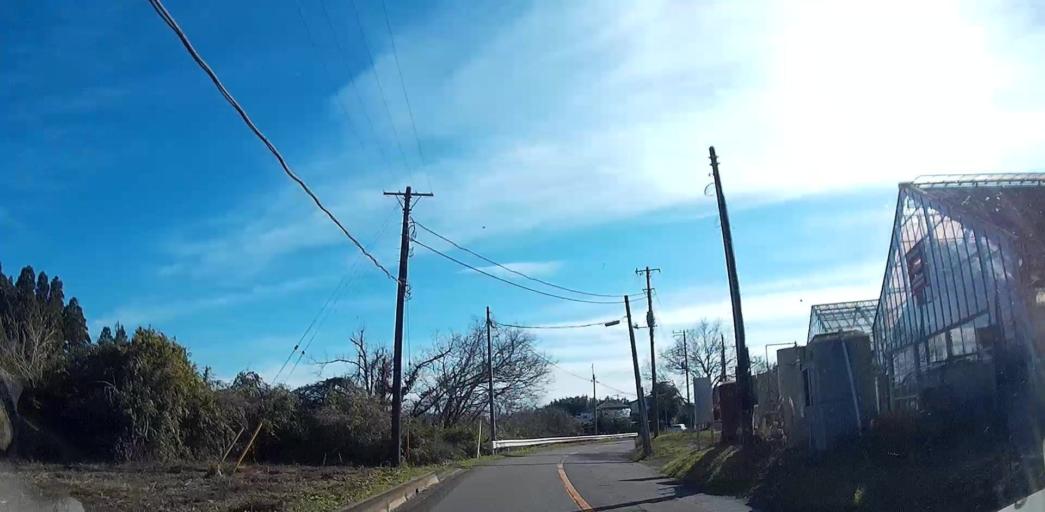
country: JP
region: Chiba
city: Yokaichiba
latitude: 35.7473
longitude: 140.4596
